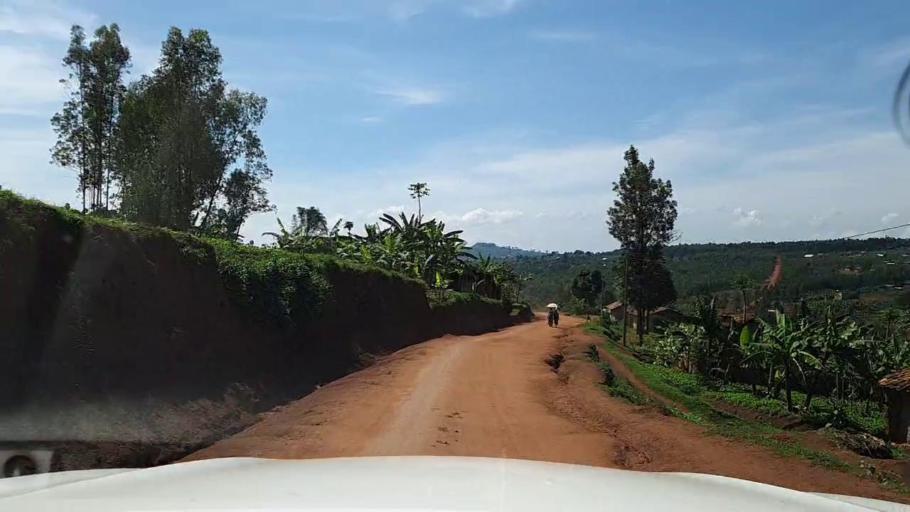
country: RW
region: Southern Province
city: Butare
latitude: -2.6950
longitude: 29.8542
